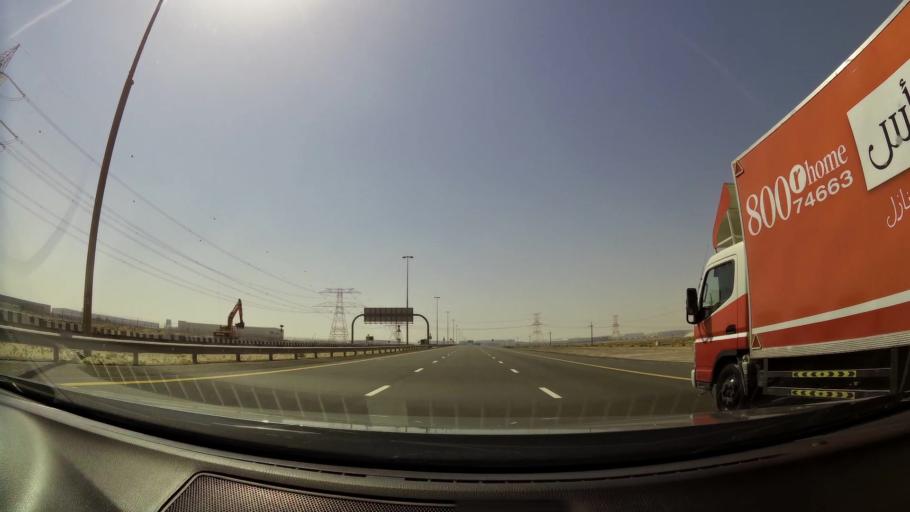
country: AE
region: Dubai
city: Dubai
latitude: 24.9260
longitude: 55.0935
